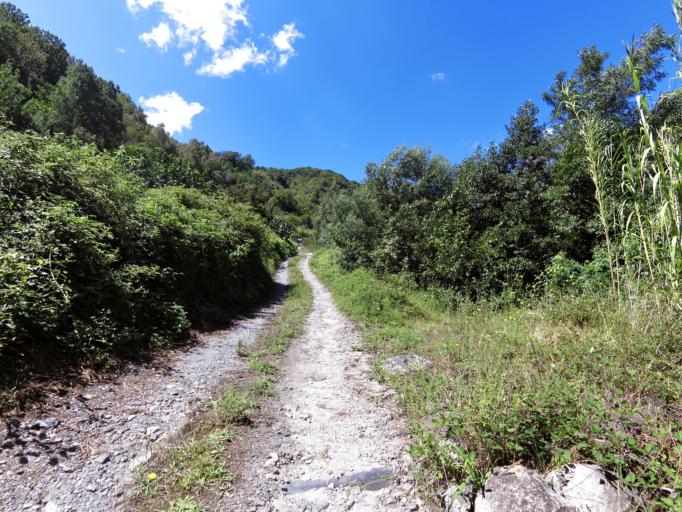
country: IT
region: Calabria
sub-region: Provincia di Reggio Calabria
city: Pazzano
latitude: 38.4749
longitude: 16.4383
